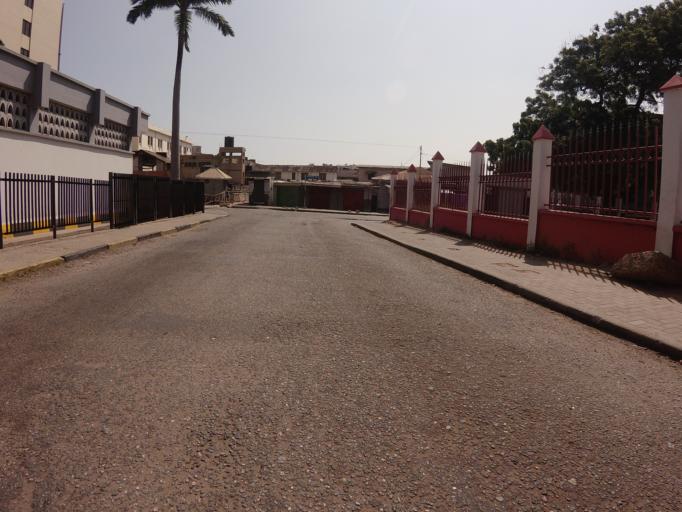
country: GH
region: Greater Accra
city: Accra
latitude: 5.5442
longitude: -0.2057
